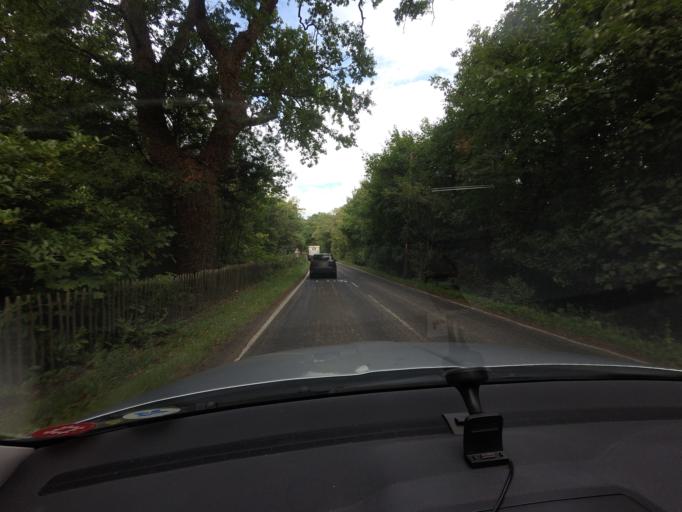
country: GB
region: England
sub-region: Kent
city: Tonbridge
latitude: 51.2345
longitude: 0.2875
